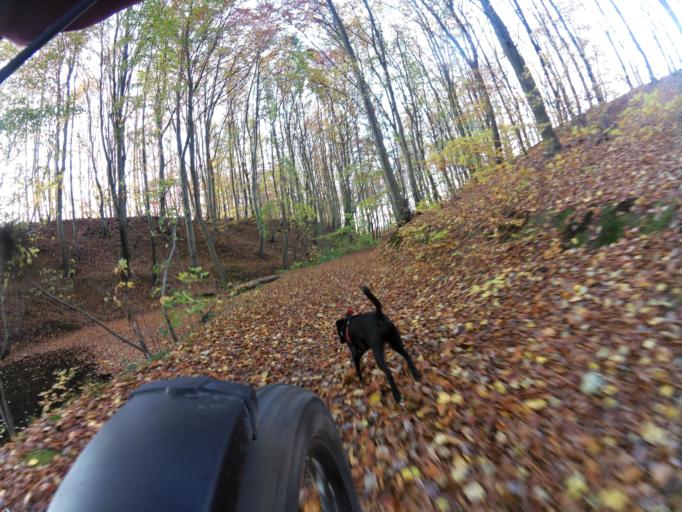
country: PL
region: Pomeranian Voivodeship
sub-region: Powiat pucki
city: Krokowa
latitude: 54.7710
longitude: 18.1739
